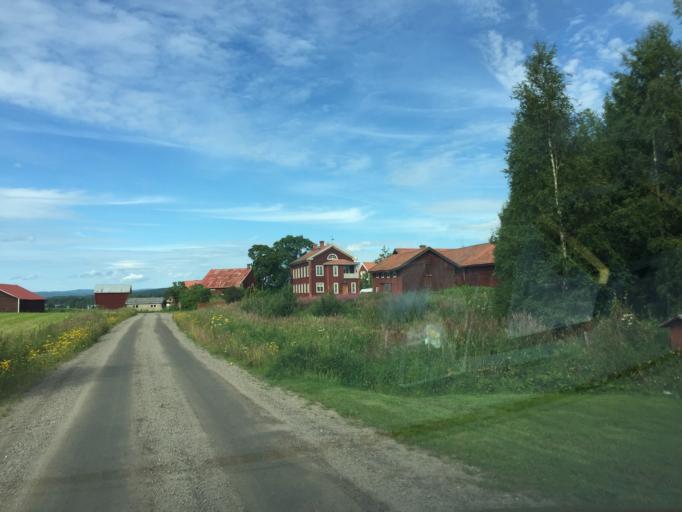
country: SE
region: Gaevleborg
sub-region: Ljusdals Kommun
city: Jaervsoe
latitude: 61.7295
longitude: 16.1728
